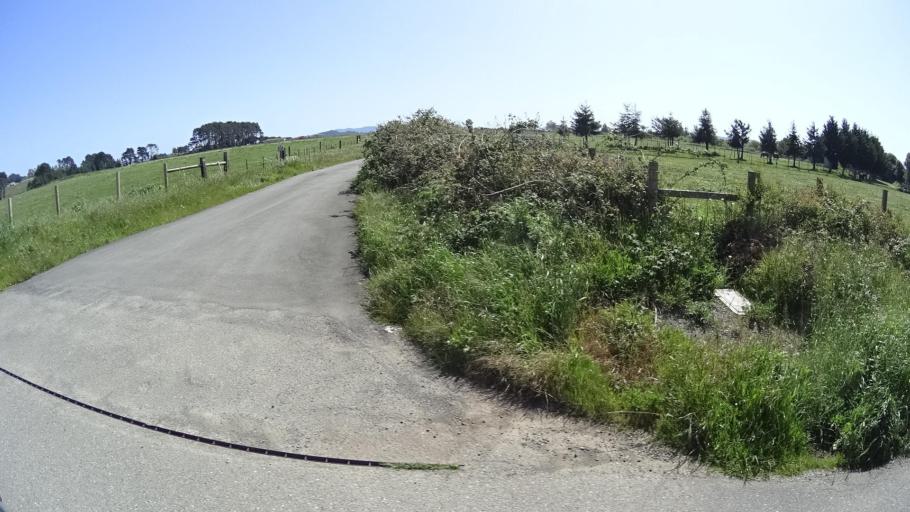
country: US
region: California
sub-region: Humboldt County
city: Fortuna
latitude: 40.5630
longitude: -124.1376
